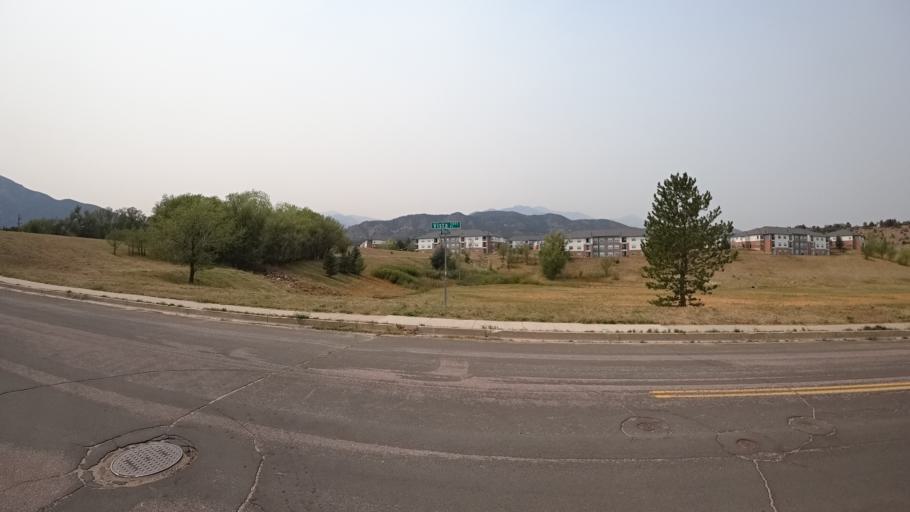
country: US
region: Colorado
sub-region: El Paso County
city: Colorado Springs
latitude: 38.8038
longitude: -104.8502
